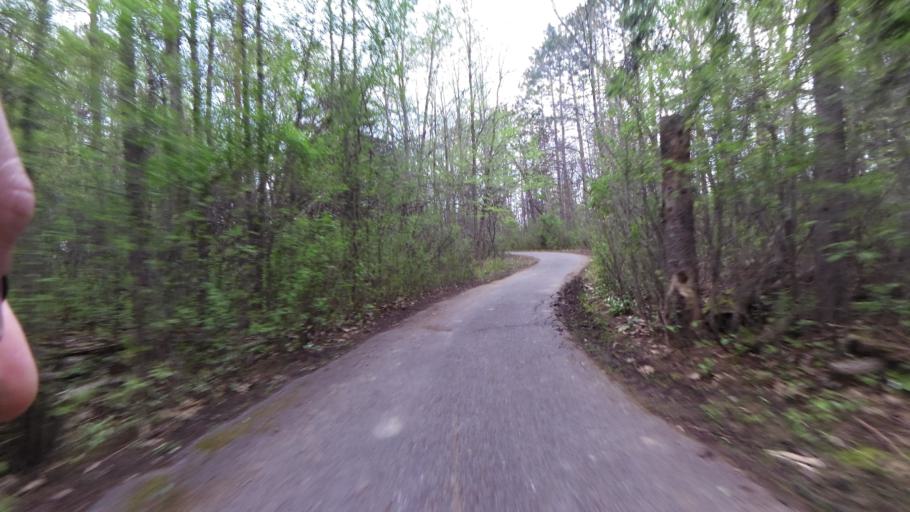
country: CA
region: Ontario
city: Bells Corners
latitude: 45.3485
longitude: -75.8463
